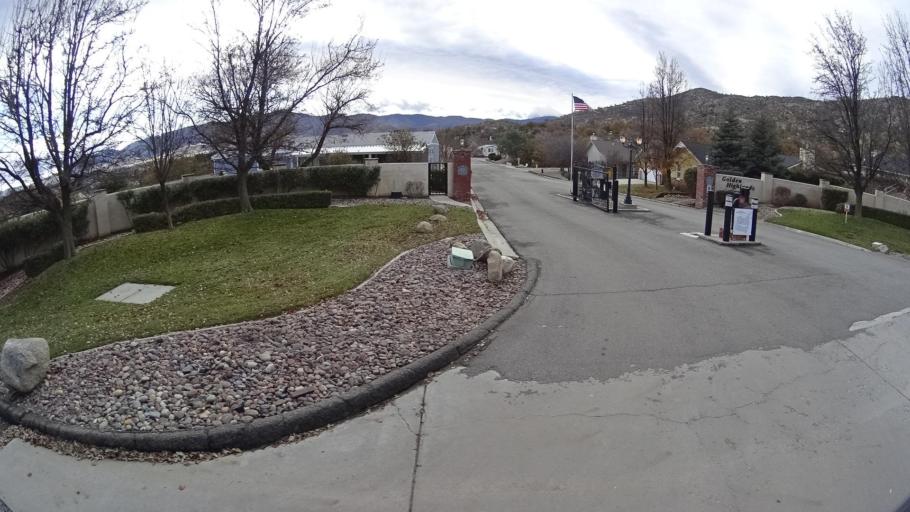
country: US
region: California
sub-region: Kern County
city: Golden Hills
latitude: 35.1547
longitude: -118.5084
